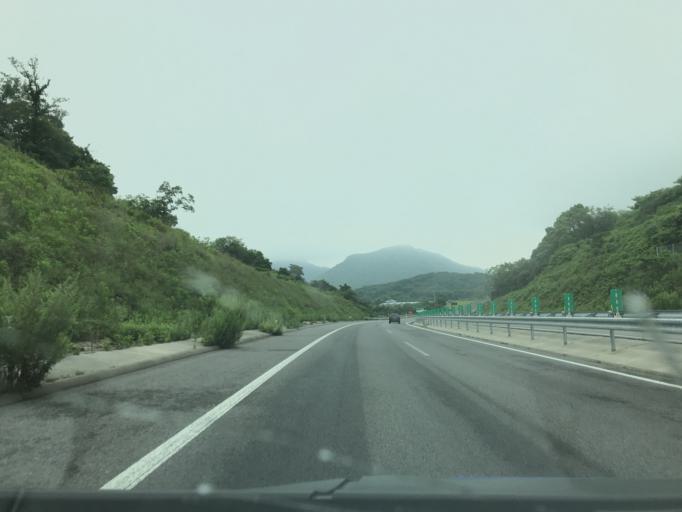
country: JP
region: Oita
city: Bungo-Takada-shi
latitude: 33.5036
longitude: 131.3101
